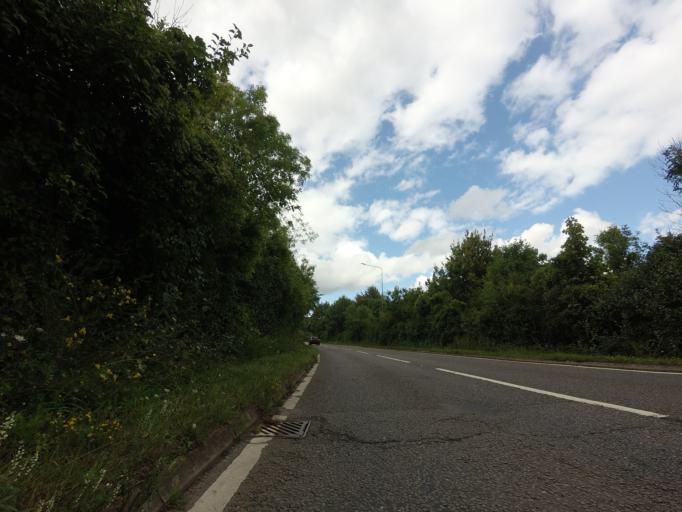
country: GB
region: England
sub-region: Kent
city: Borough Green
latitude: 51.3072
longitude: 0.3178
